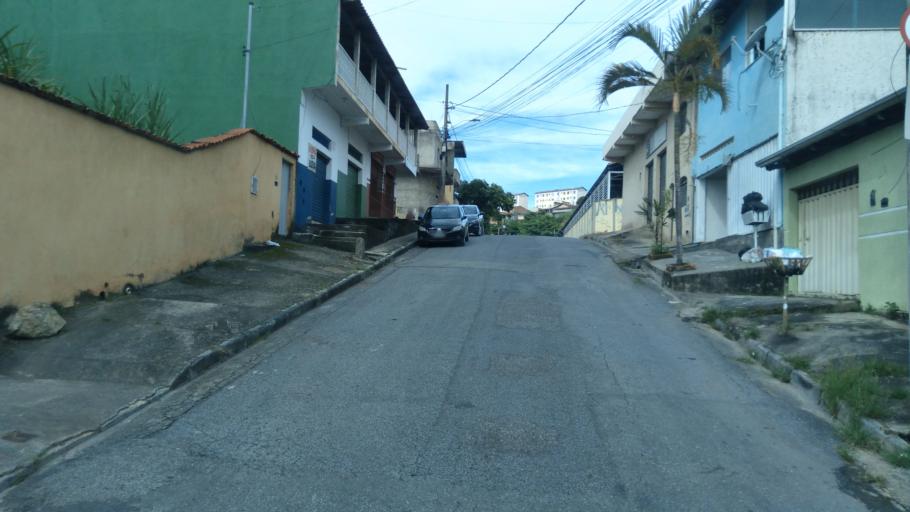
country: BR
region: Minas Gerais
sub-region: Santa Luzia
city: Santa Luzia
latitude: -19.8450
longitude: -43.8939
